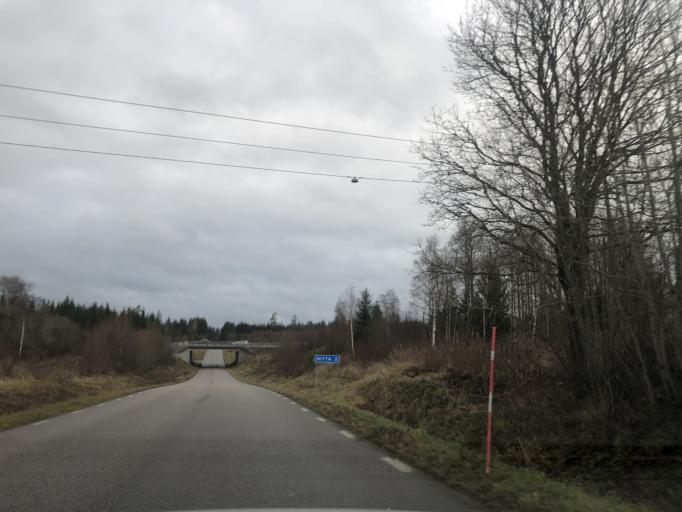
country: SE
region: Vaestra Goetaland
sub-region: Boras Kommun
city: Dalsjofors
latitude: 57.8074
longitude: 13.1979
